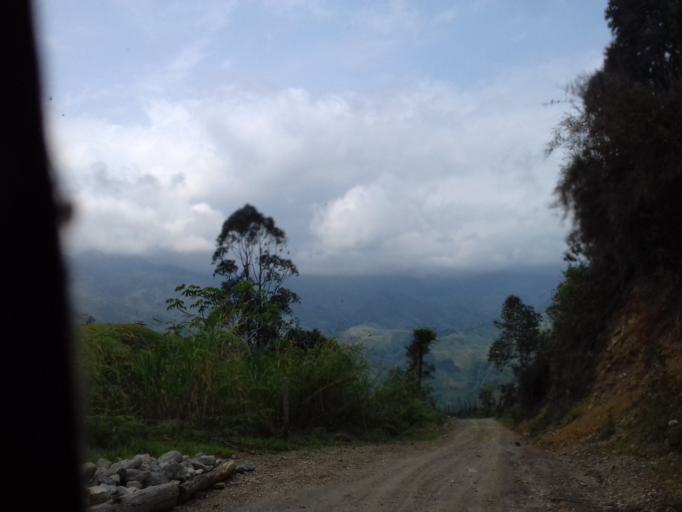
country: CO
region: Tolima
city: Libano
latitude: 4.9358
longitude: -75.0708
